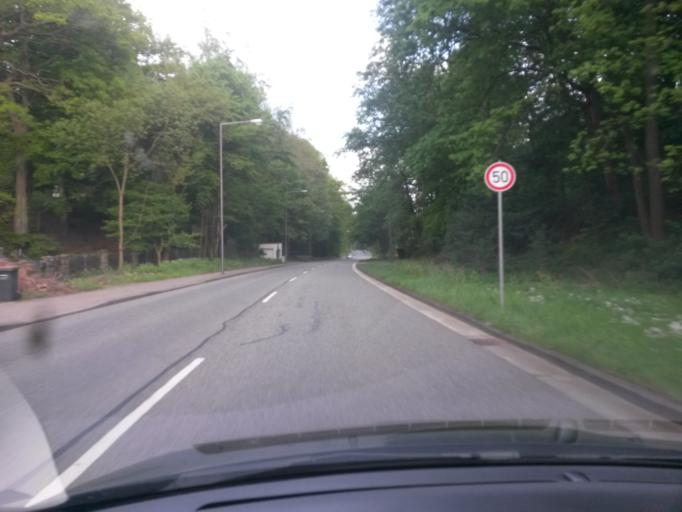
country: DE
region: Hesse
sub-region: Regierungsbezirk Kassel
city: Baunatal
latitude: 51.3088
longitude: 9.3910
